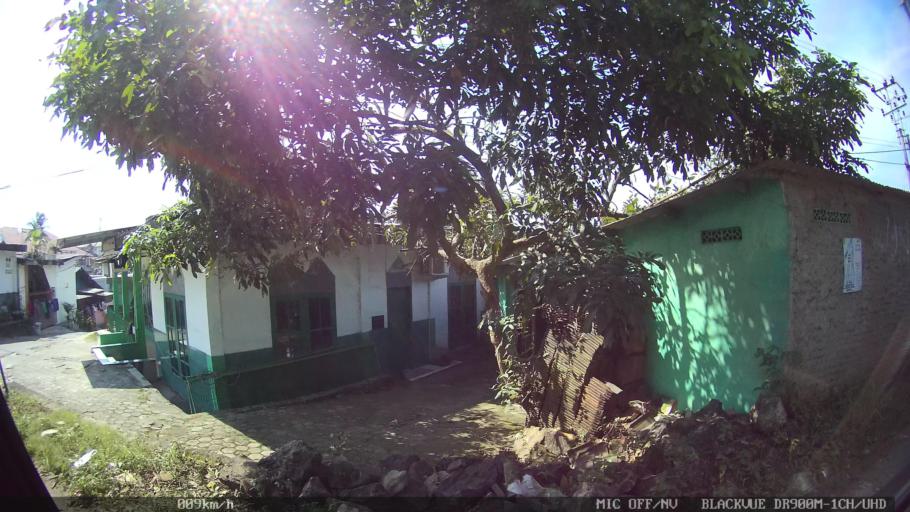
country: ID
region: Lampung
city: Kedaton
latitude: -5.3598
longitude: 105.2420
